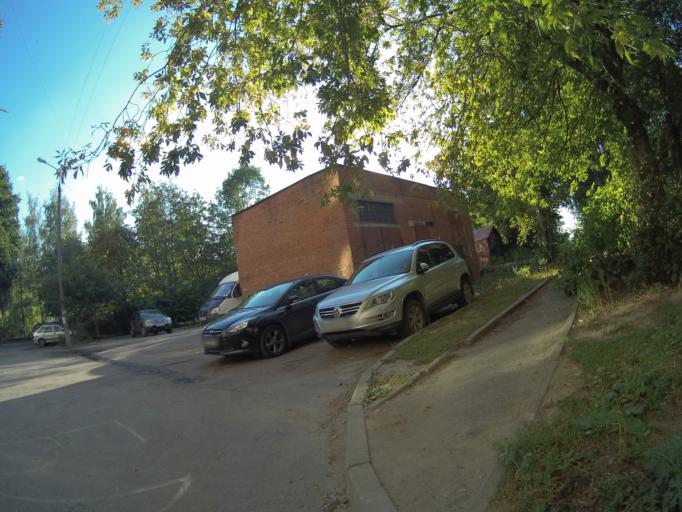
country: RU
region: Vladimir
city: Vladimir
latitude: 56.1510
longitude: 40.3690
